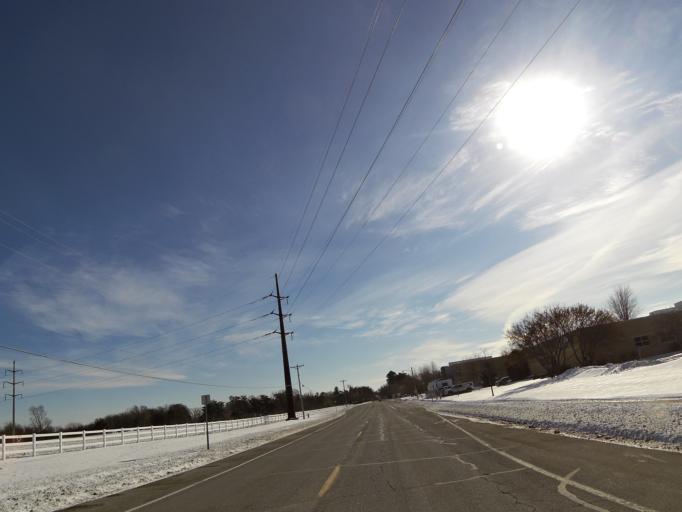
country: US
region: Minnesota
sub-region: Dakota County
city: Hastings
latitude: 44.7488
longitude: -92.8747
